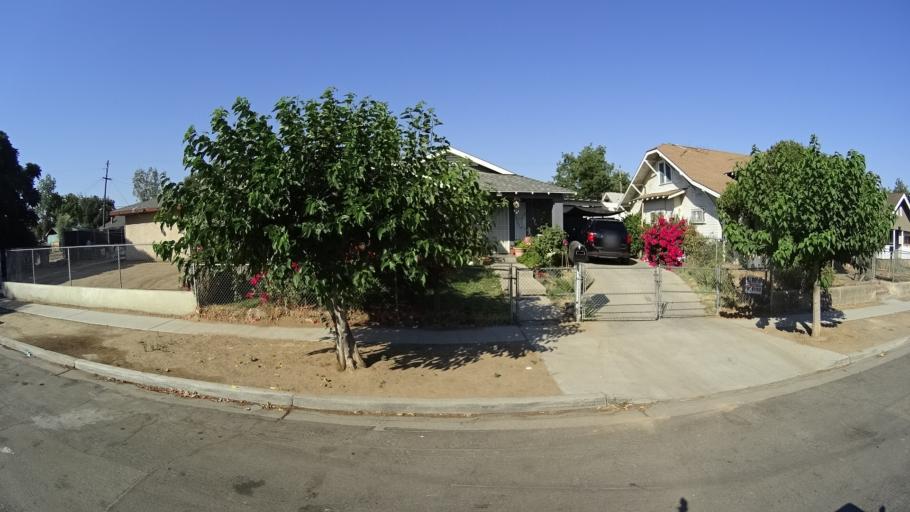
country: US
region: California
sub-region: Fresno County
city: Fresno
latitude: 36.7260
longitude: -119.7973
